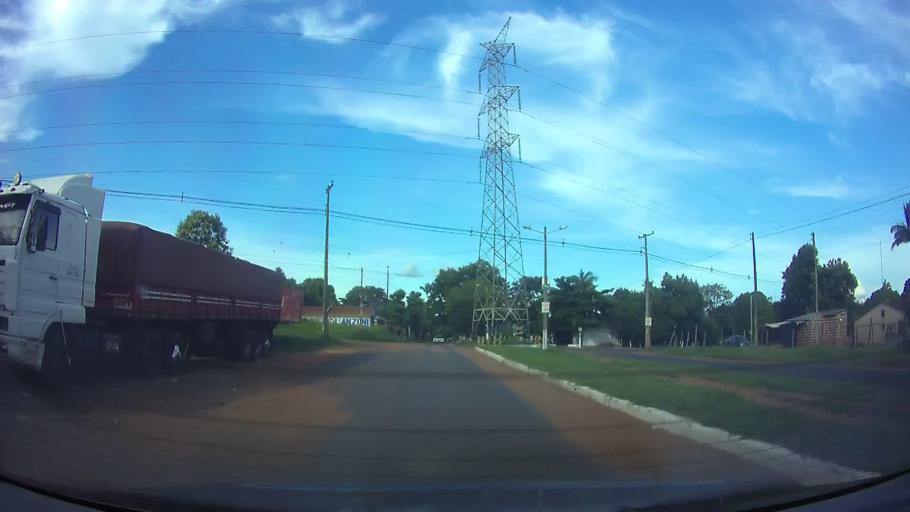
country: PY
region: Central
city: San Antonio
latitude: -25.4237
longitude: -57.5411
